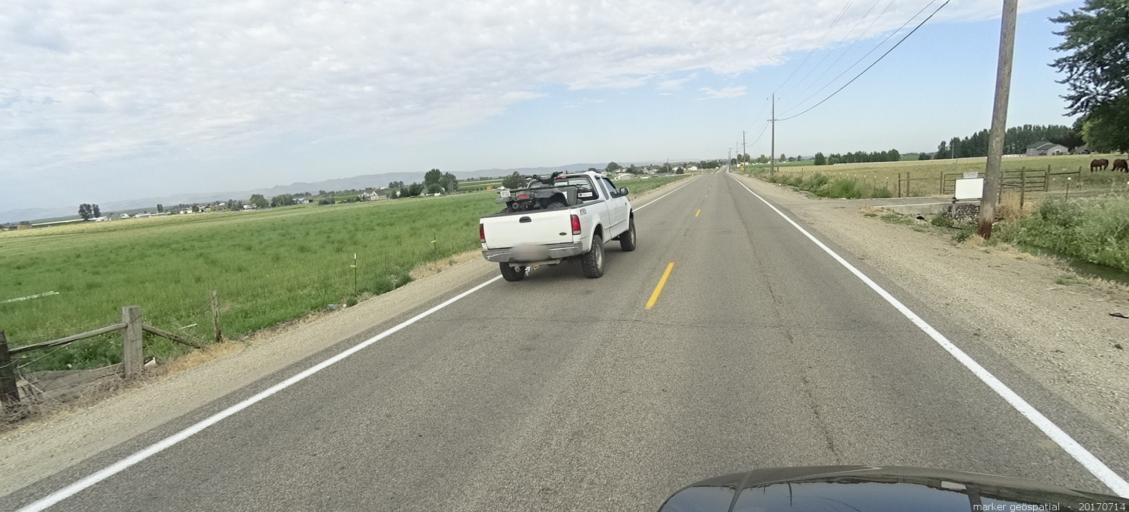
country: US
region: Idaho
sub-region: Ada County
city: Kuna
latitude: 43.4883
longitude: -116.4692
